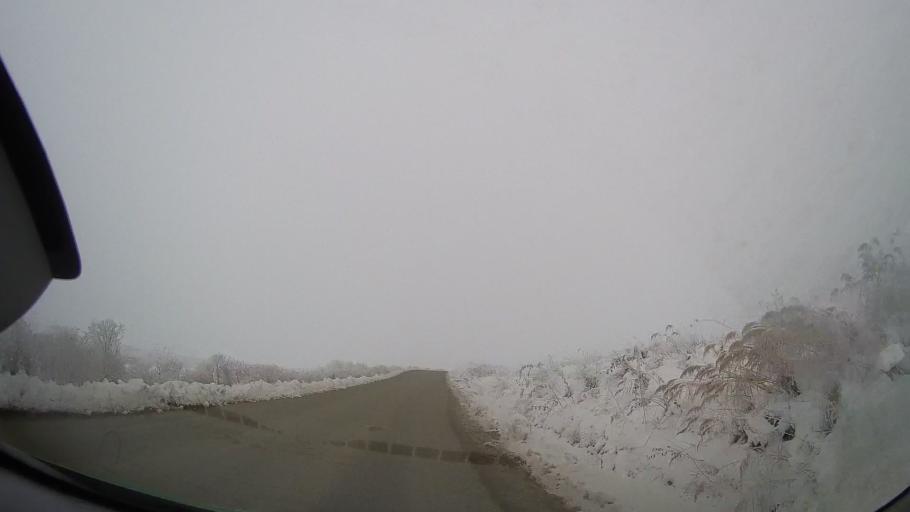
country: RO
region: Iasi
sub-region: Comuna Tansa
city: Suhulet
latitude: 46.8850
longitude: 27.2758
